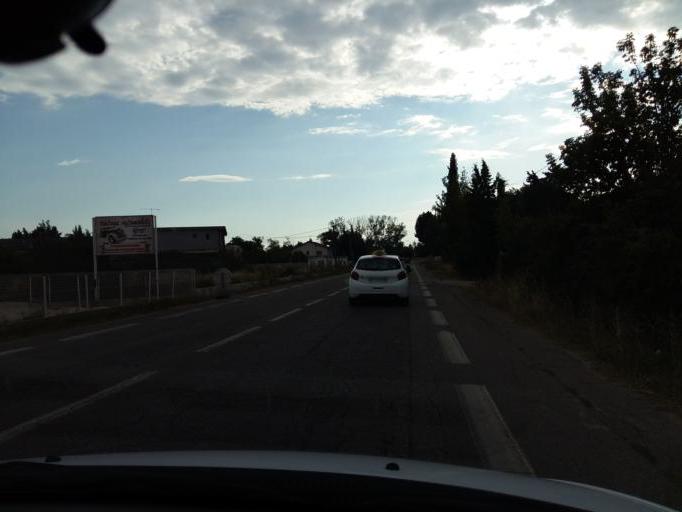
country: FR
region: Provence-Alpes-Cote d'Azur
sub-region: Departement du Vaucluse
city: Morieres-les-Avignon
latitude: 43.9532
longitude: 4.8879
